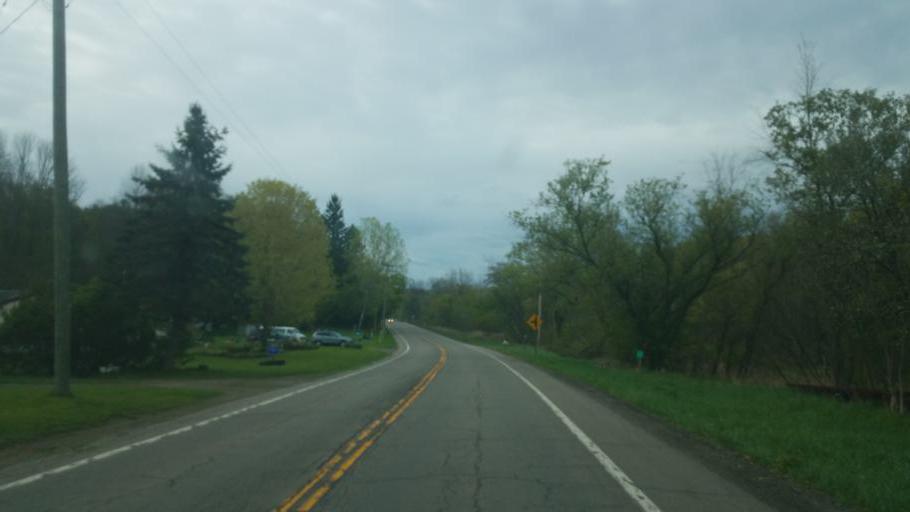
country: US
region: New York
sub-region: Steuben County
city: Canisteo
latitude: 42.2055
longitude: -77.5600
